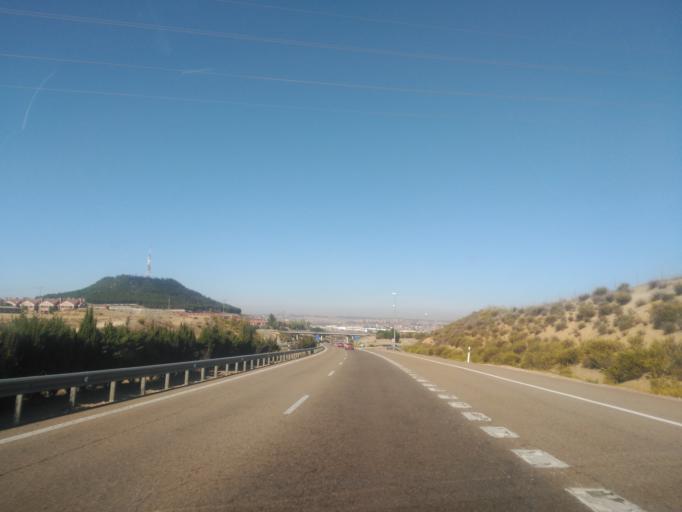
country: ES
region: Castille and Leon
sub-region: Provincia de Valladolid
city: Cisterniga
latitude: 41.6157
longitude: -4.6797
